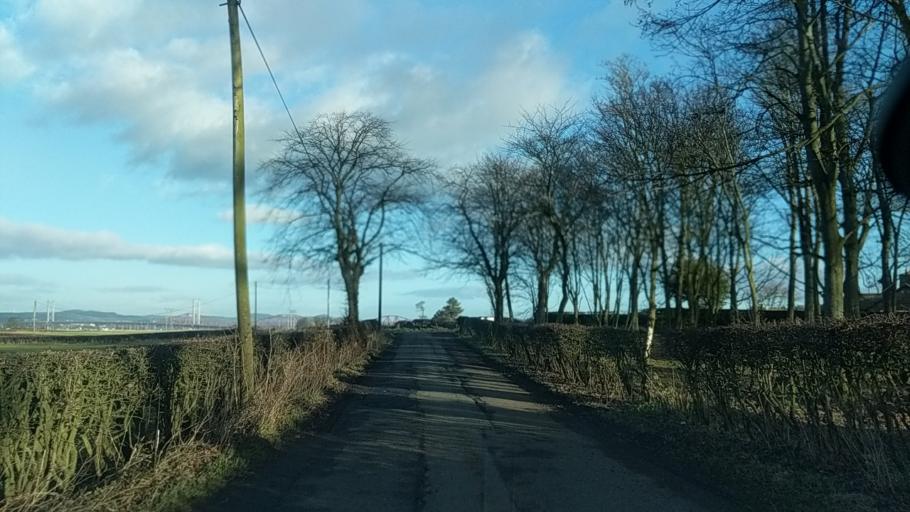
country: GB
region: Scotland
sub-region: Edinburgh
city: Queensferry
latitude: 55.9765
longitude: -3.4349
